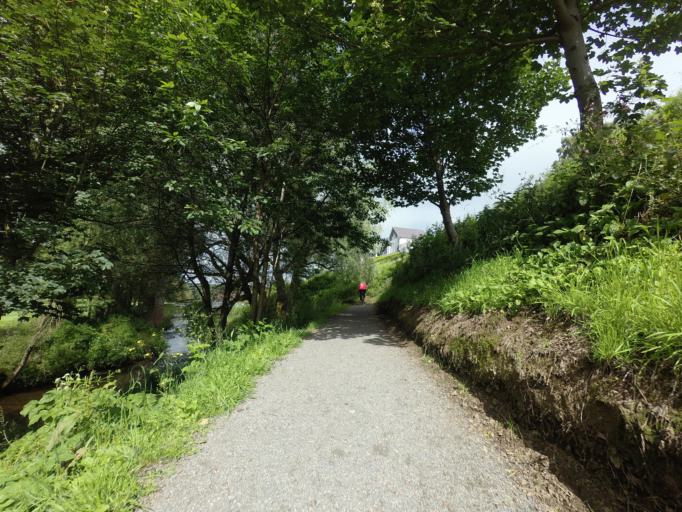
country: GB
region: Scotland
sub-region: Aberdeenshire
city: Turriff
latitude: 57.5383
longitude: -2.4707
